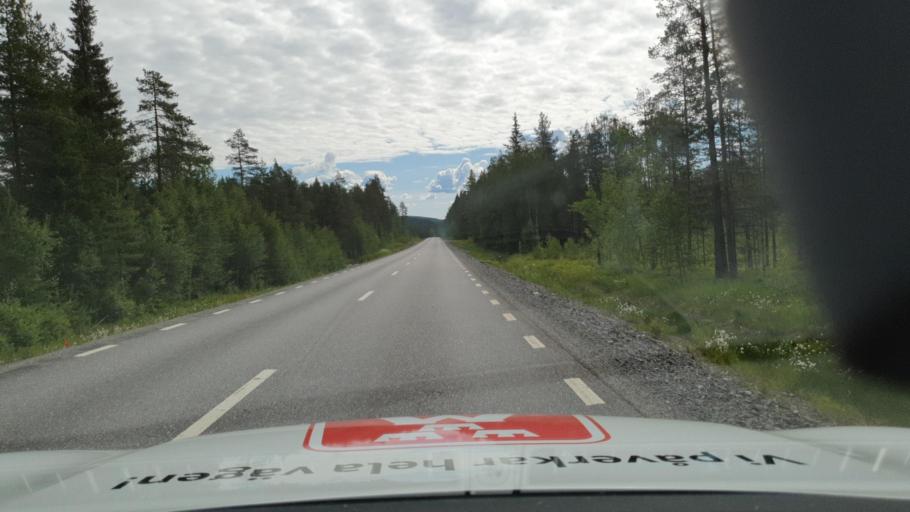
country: SE
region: Vaesterbotten
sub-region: Umea Kommun
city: Ersmark
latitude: 64.2591
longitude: 20.1863
